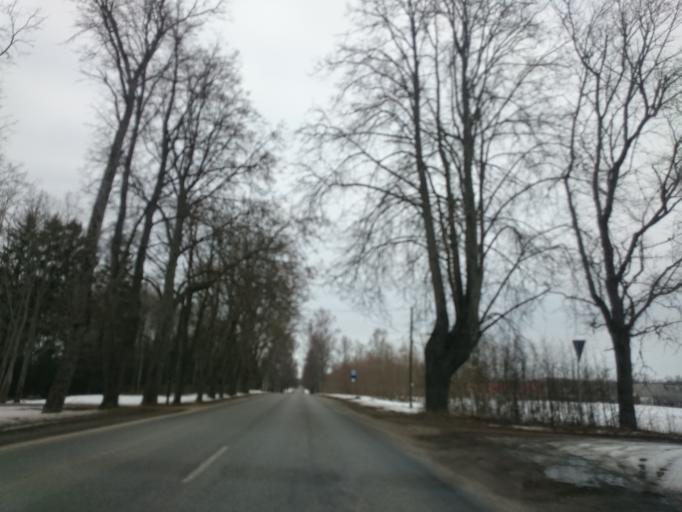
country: LV
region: Cesu Rajons
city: Cesis
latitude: 57.2883
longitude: 25.2663
